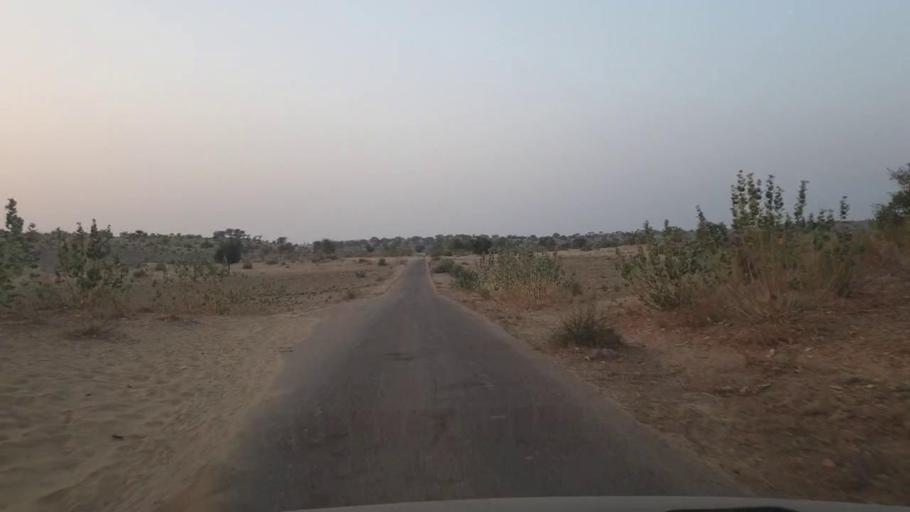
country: PK
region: Sindh
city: Umarkot
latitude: 25.3038
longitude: 70.0719
